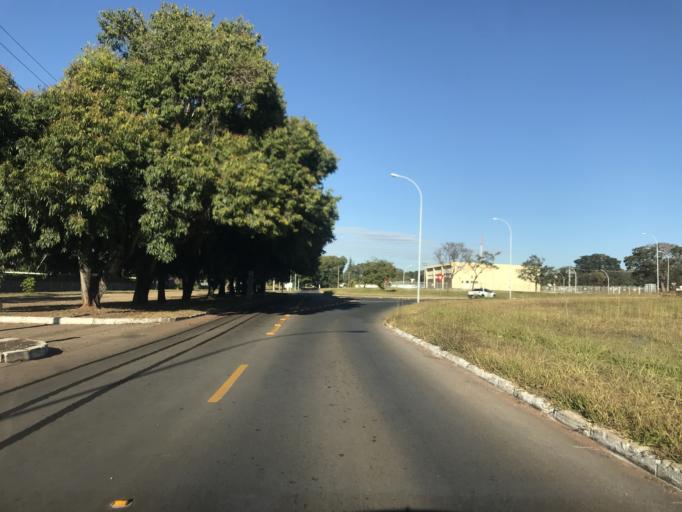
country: BR
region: Federal District
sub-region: Brasilia
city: Brasilia
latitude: -15.8219
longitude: -47.8890
